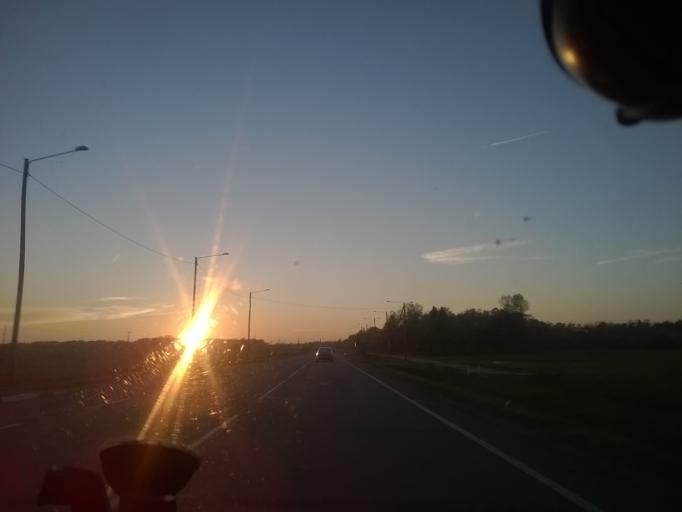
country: EE
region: Laeaene
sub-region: Ridala Parish
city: Uuemoisa
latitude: 58.9561
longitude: 23.7748
